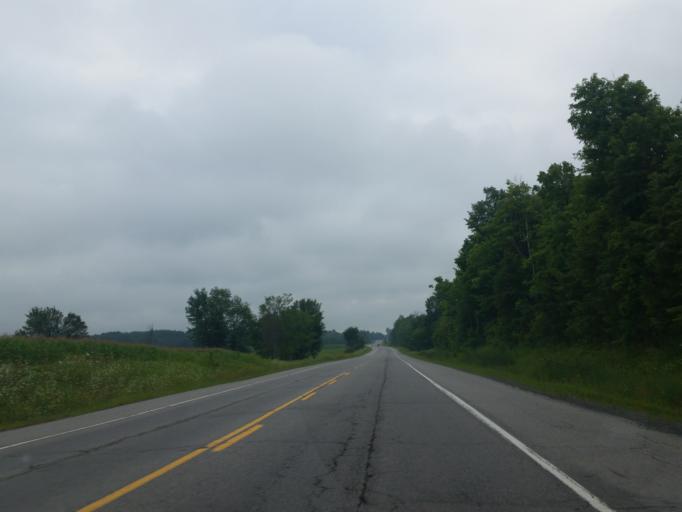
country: CA
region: Ontario
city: Clarence-Rockland
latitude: 45.3912
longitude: -75.3909
